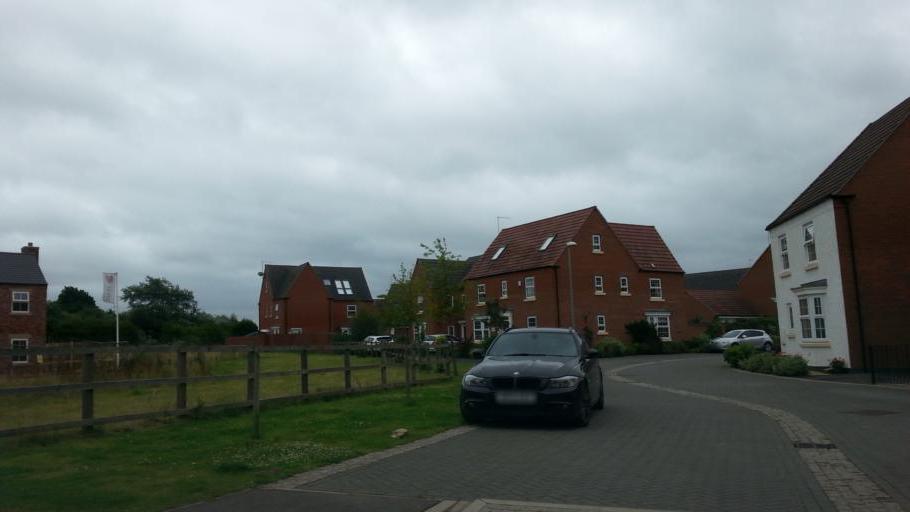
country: GB
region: England
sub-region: Nottinghamshire
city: Hucknall
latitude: 53.0462
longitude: -1.1858
